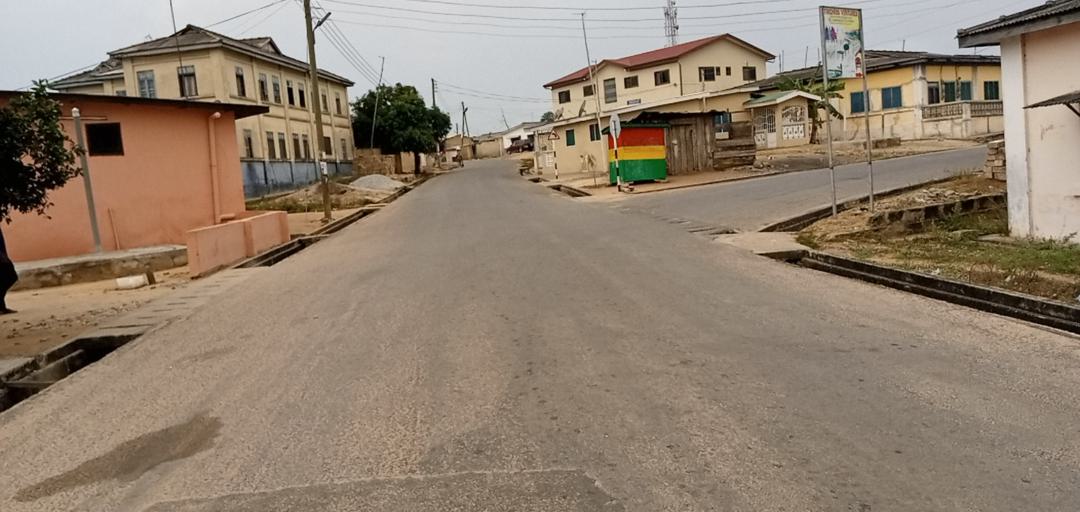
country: GH
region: Central
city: Winneba
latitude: 5.3505
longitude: -0.6226
